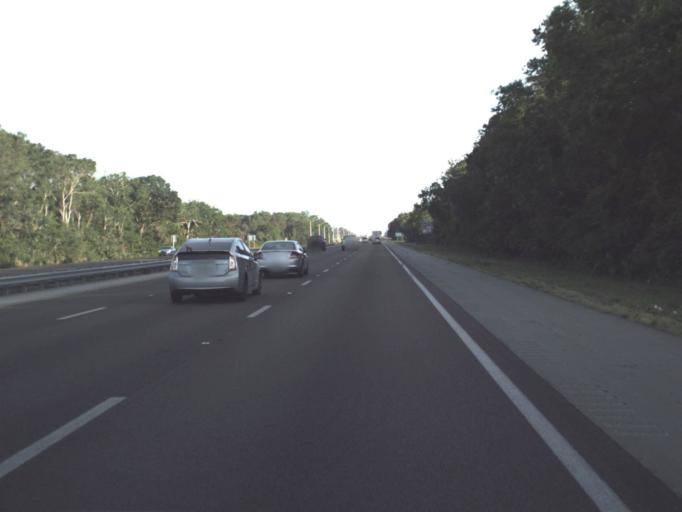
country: US
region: Florida
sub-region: Brevard County
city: Mims
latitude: 28.6793
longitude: -80.8753
